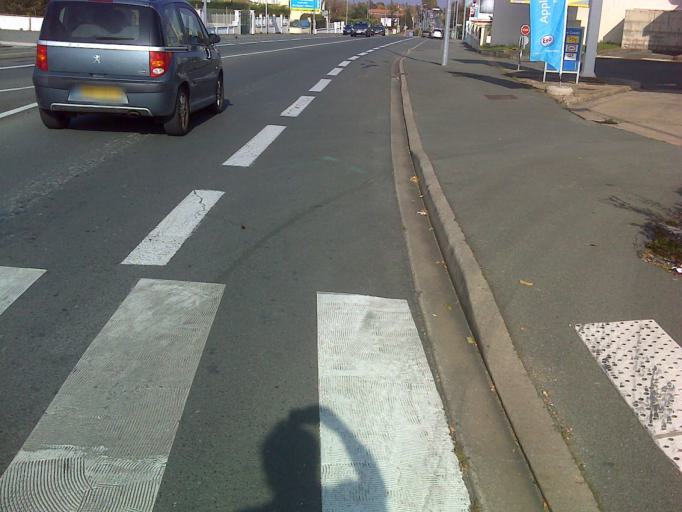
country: FR
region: Poitou-Charentes
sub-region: Departement de la Charente-Maritime
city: Rochefort
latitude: 45.9480
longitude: -0.9764
